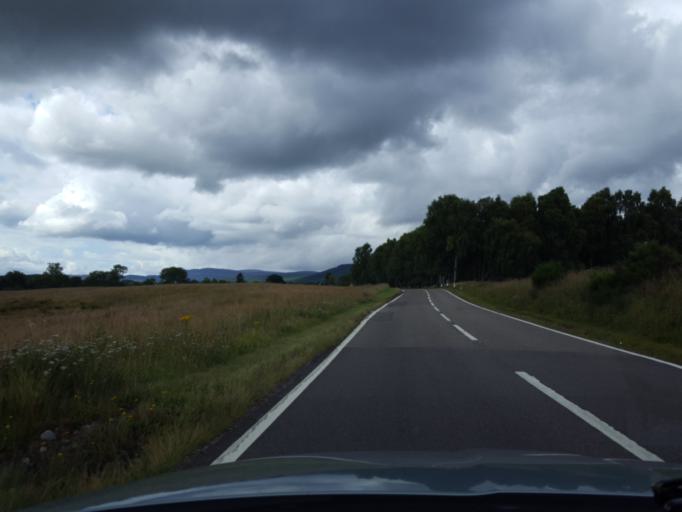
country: GB
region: Scotland
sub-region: Highland
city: Aviemore
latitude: 57.2638
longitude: -3.7339
